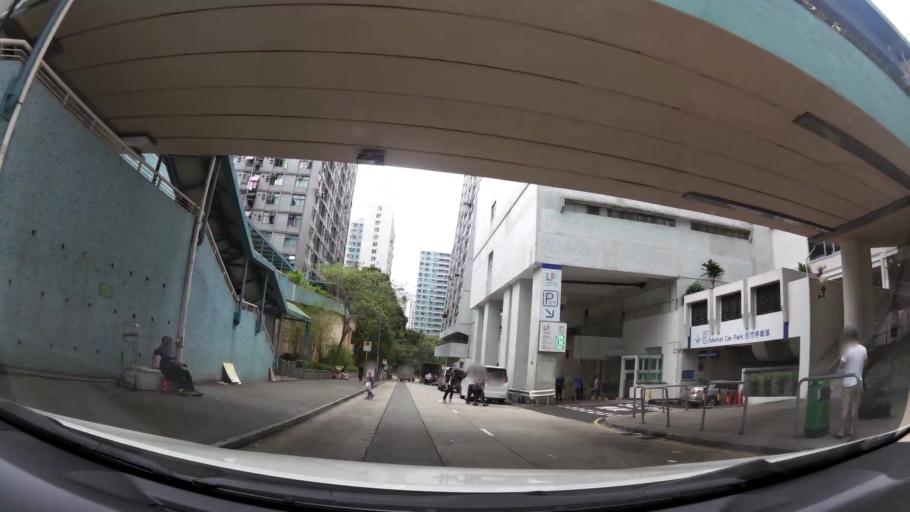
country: HK
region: Wong Tai Sin
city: Wong Tai Sin
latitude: 22.3397
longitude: 114.1869
